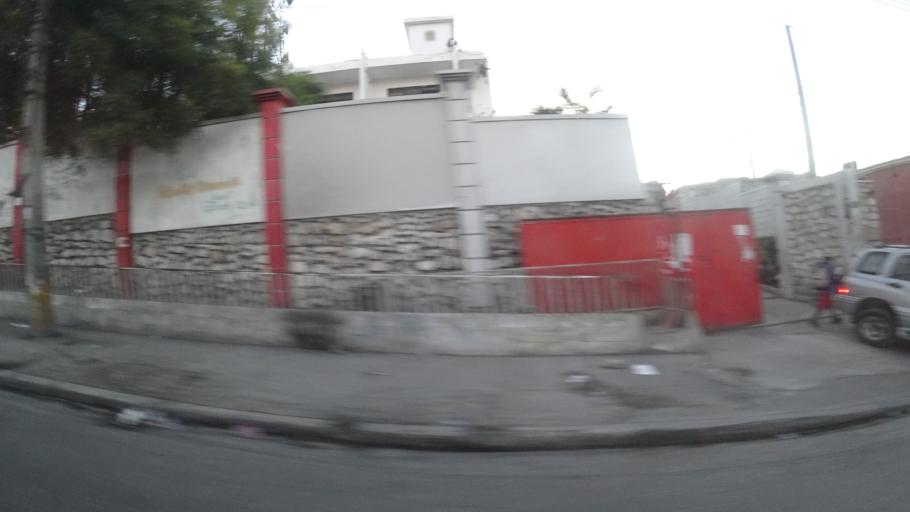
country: HT
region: Ouest
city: Delmas 73
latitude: 18.5493
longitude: -72.3168
